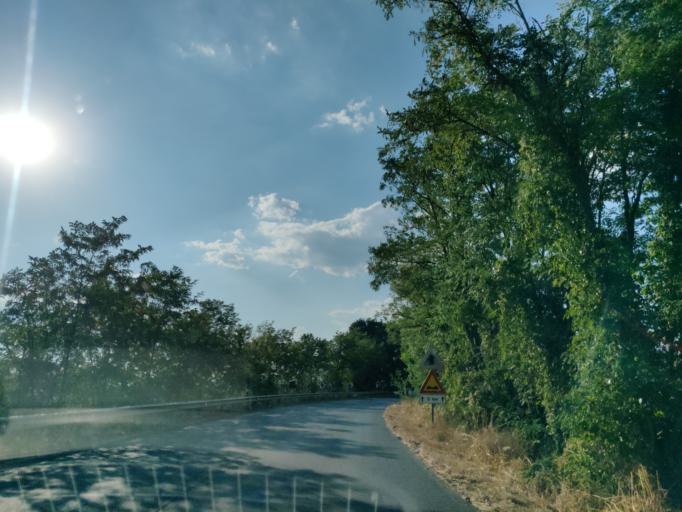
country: IT
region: Latium
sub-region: Provincia di Viterbo
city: Proceno
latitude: 42.7814
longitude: 11.8337
